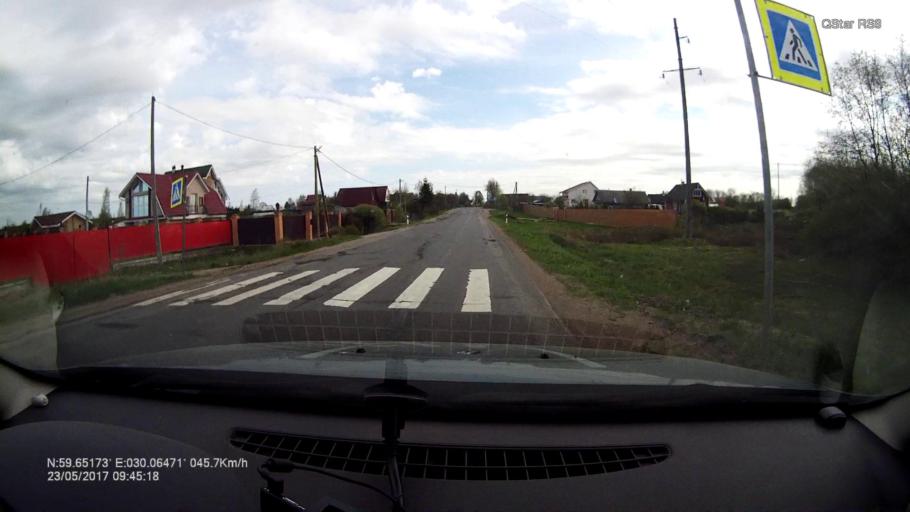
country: RU
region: Leningrad
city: Taytsy
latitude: 59.6518
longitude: 30.0650
